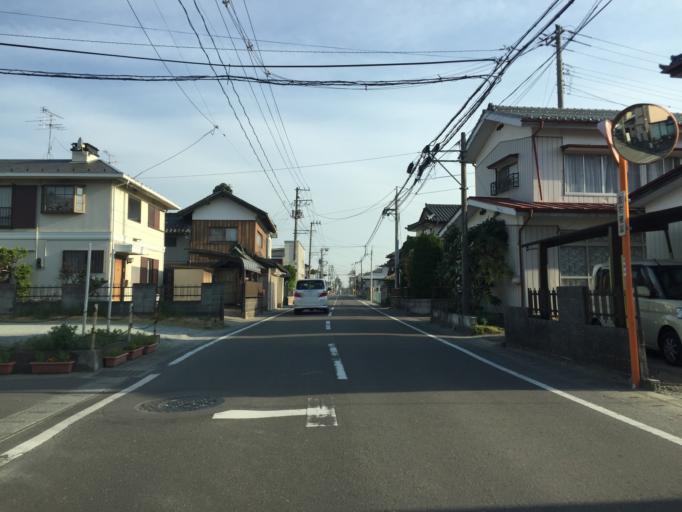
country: JP
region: Miyagi
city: Watari
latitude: 38.0305
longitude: 140.8543
